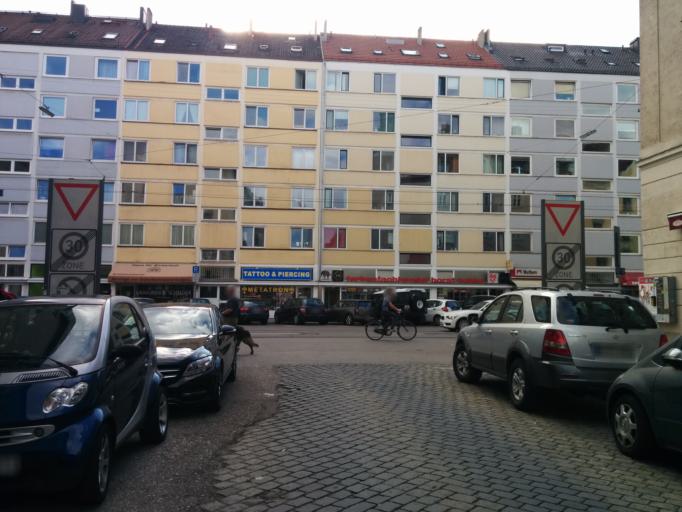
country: DE
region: Bavaria
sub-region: Upper Bavaria
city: Munich
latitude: 48.1619
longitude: 11.5752
